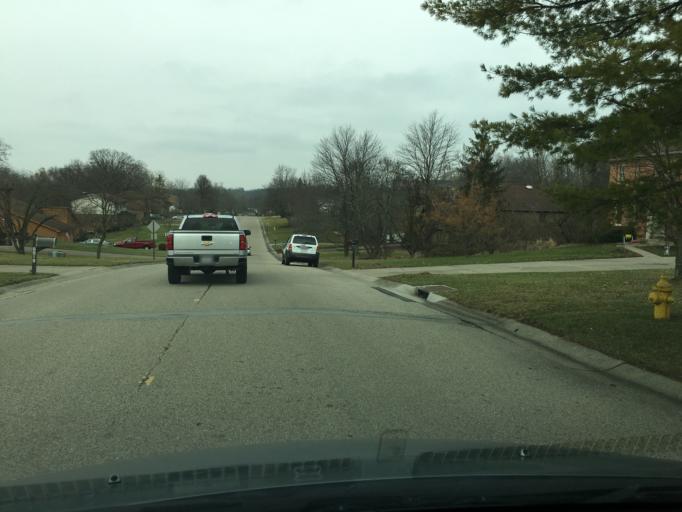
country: US
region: Ohio
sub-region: Hamilton County
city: Sharonville
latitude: 39.3001
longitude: -84.3993
